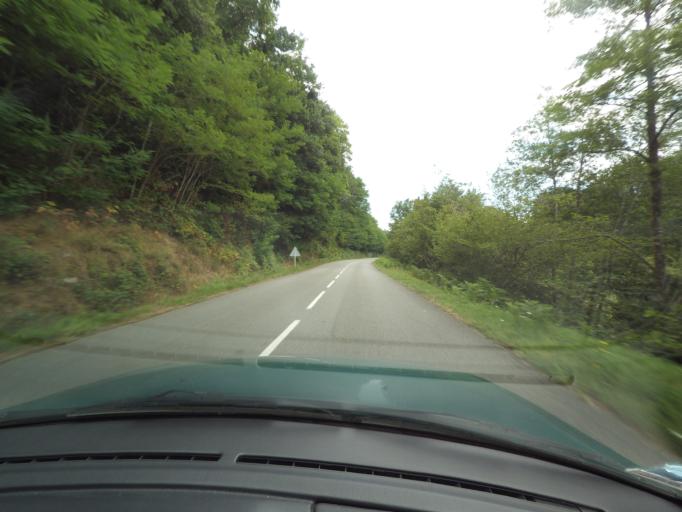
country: FR
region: Limousin
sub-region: Departement de la Haute-Vienne
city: Eymoutiers
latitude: 45.7167
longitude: 1.8133
